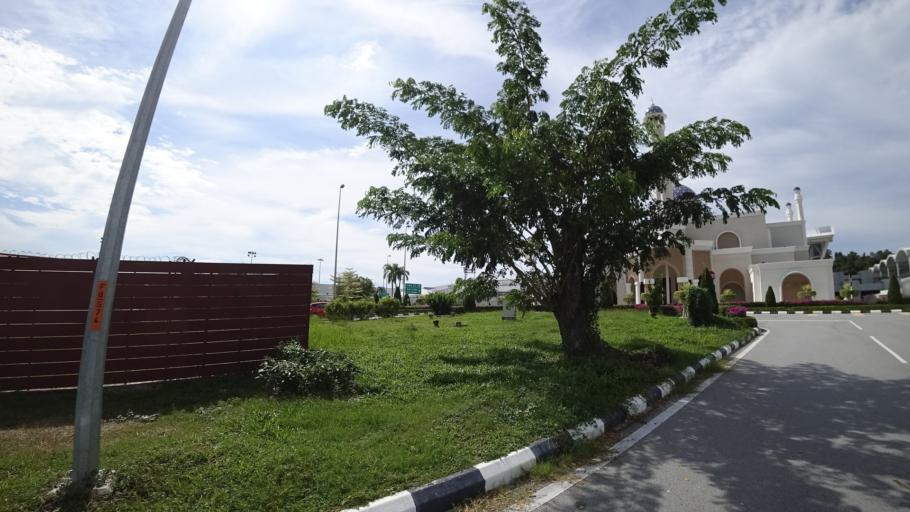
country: BN
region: Brunei and Muara
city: Bandar Seri Begawan
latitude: 4.9433
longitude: 114.9337
